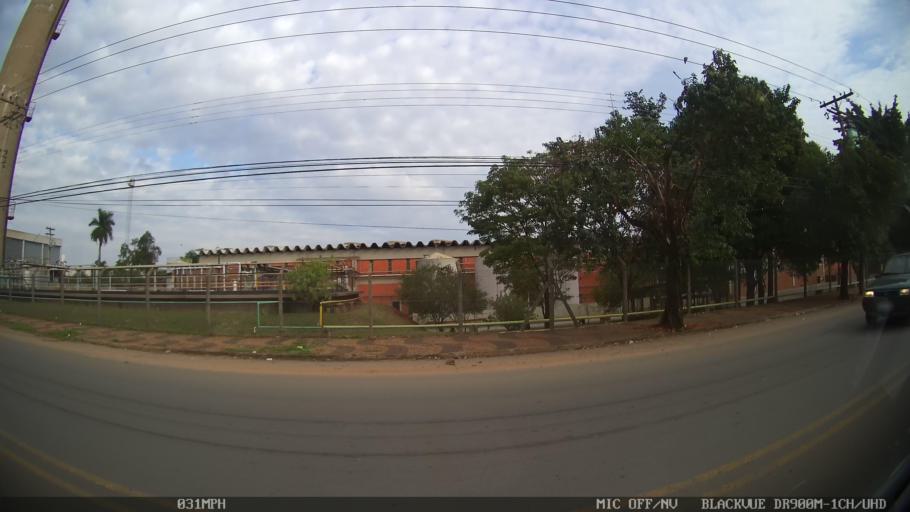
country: BR
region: Sao Paulo
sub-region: Santa Barbara D'Oeste
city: Santa Barbara d'Oeste
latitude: -22.7561
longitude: -47.3864
